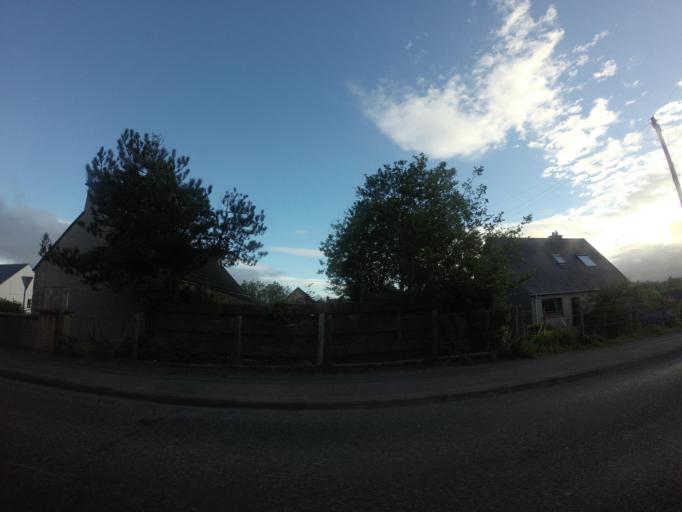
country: GB
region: Scotland
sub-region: Eilean Siar
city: Stornoway
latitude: 58.2059
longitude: -6.3552
